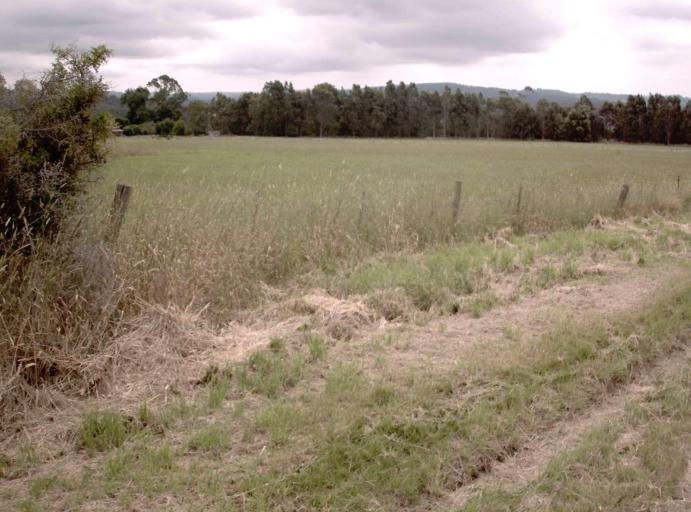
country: AU
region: Victoria
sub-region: Latrobe
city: Traralgon
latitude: -38.5129
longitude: 146.6624
